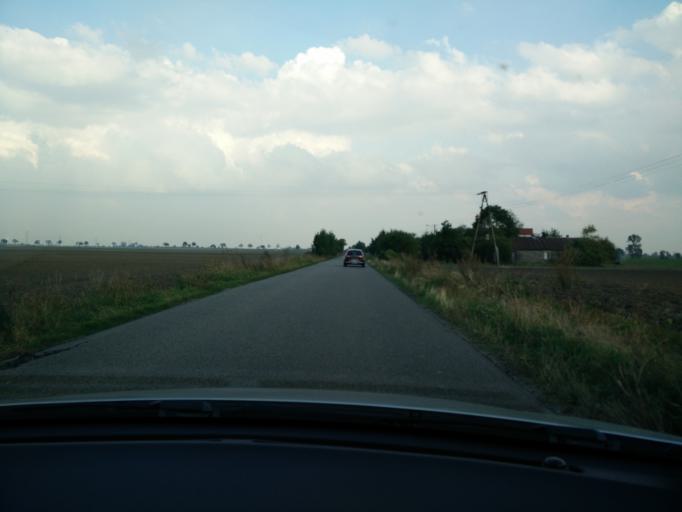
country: PL
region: Greater Poland Voivodeship
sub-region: Powiat wrzesinski
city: Wrzesnia
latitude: 52.2830
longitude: 17.5286
